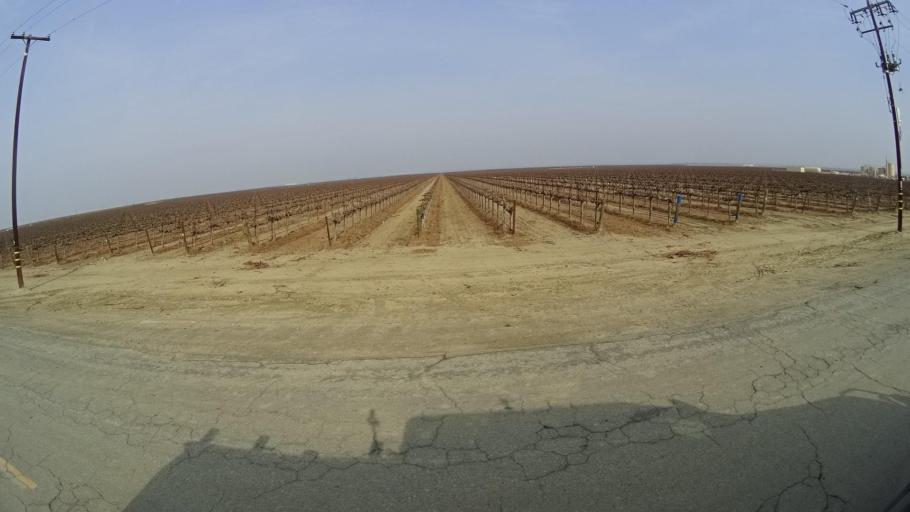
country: US
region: California
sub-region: Kern County
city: Greenfield
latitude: 35.0761
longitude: -119.0943
